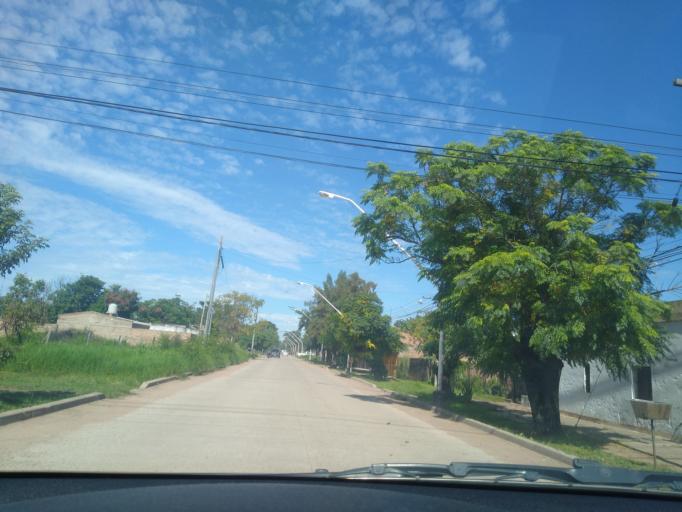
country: AR
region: Chaco
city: Presidencia Roque Saenz Pena
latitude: -26.7721
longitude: -60.4230
